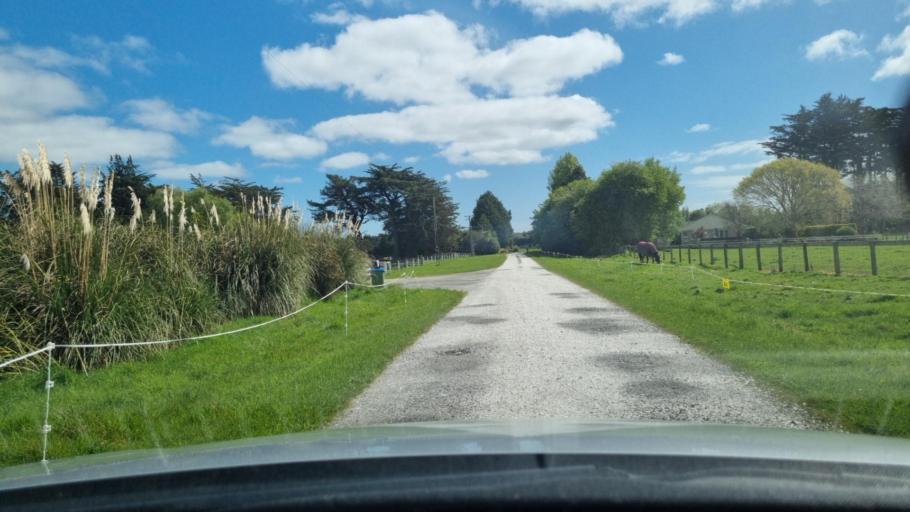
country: NZ
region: Southland
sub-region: Invercargill City
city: Invercargill
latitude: -46.3781
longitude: 168.4450
